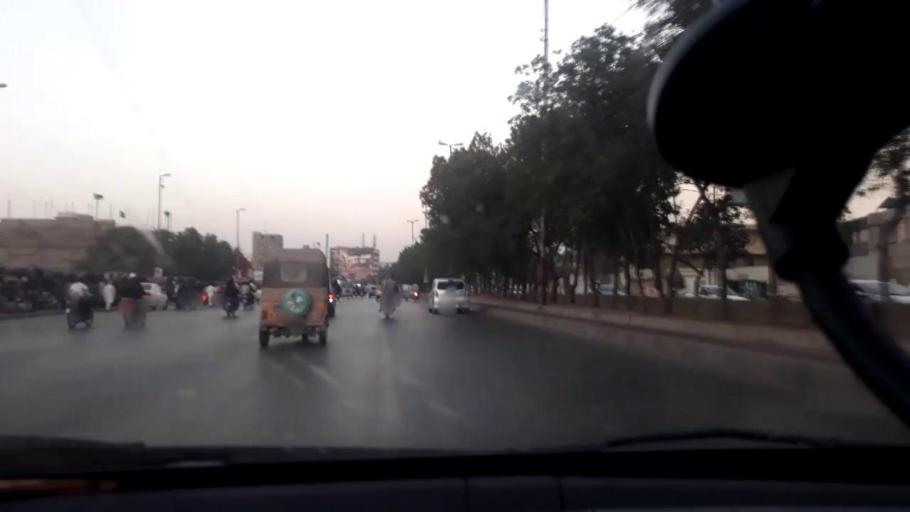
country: PK
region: Sindh
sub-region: Karachi District
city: Karachi
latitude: 24.8941
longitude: 67.0643
